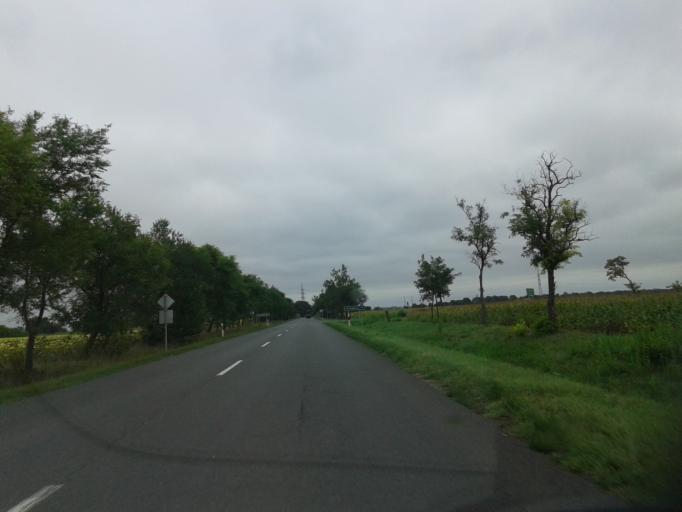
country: HU
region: Bacs-Kiskun
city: Solt
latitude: 46.8470
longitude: 18.9994
